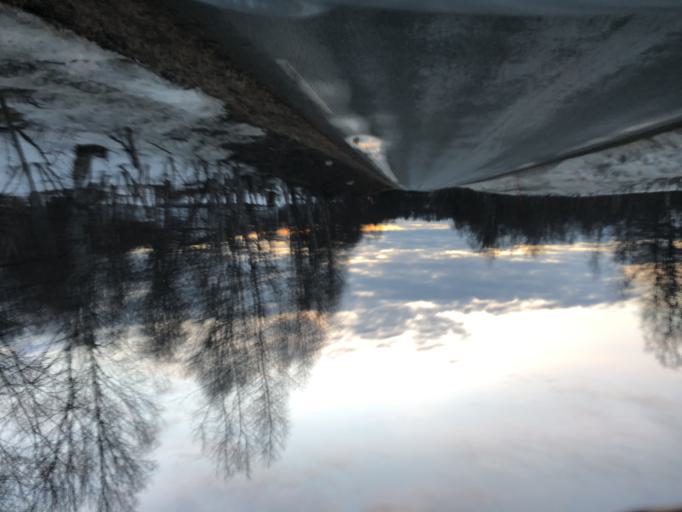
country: NO
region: Sor-Trondelag
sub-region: Tydal
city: Aas
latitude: 62.6743
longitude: 11.8071
